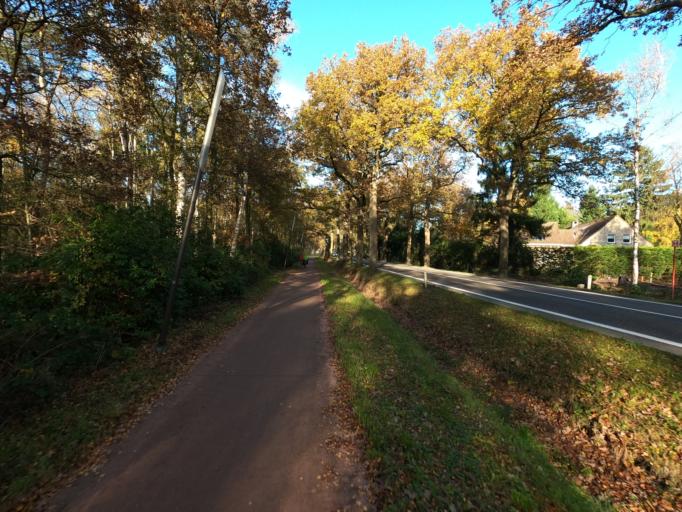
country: BE
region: Flanders
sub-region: Provincie Antwerpen
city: Brasschaat
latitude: 51.3351
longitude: 4.5189
